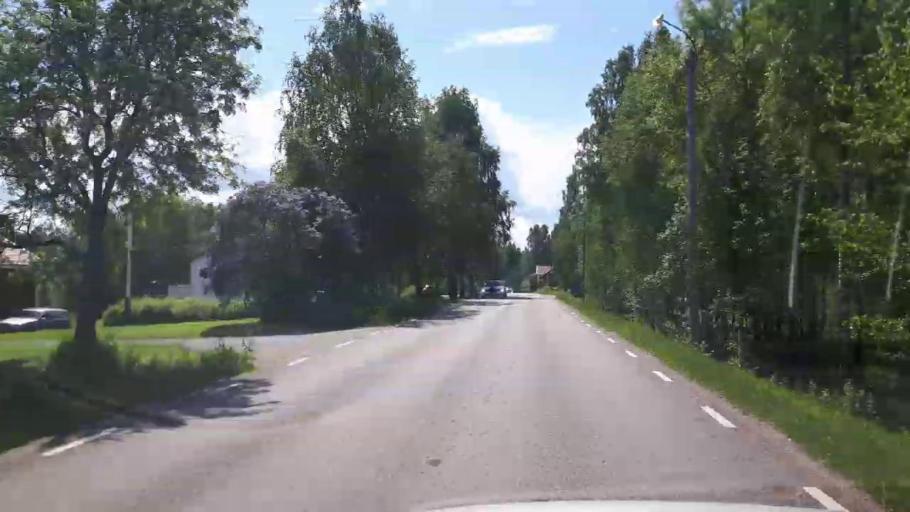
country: SE
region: Dalarna
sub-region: Faluns Kommun
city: Falun
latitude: 60.5985
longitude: 15.7656
